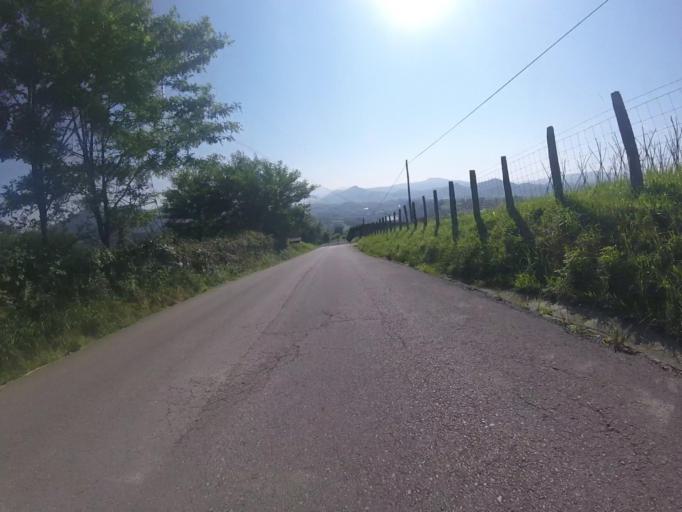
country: ES
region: Basque Country
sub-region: Provincia de Guipuzcoa
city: Astigarraga
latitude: 43.2642
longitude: -1.9369
